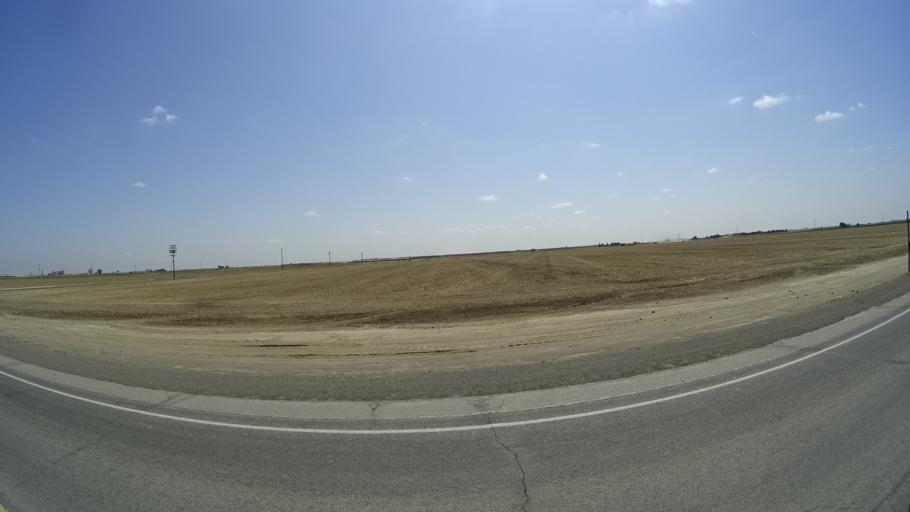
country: US
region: California
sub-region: Kings County
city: Home Garden
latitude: 36.2507
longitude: -119.6369
